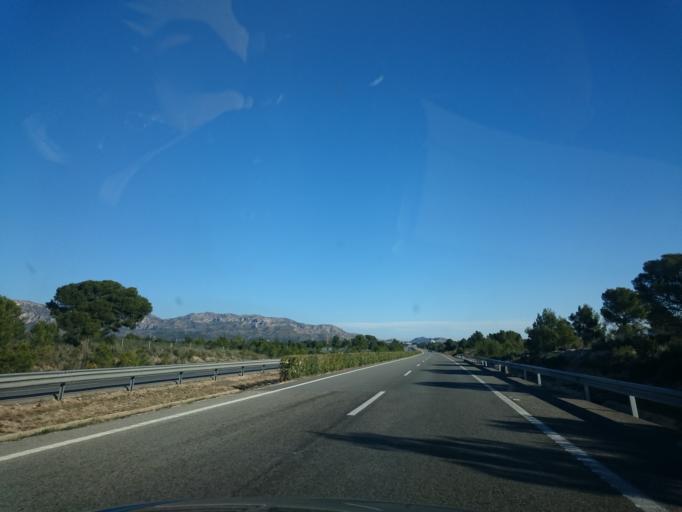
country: ES
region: Catalonia
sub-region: Provincia de Tarragona
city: l'Ametlla de Mar
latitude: 40.9096
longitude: 0.8220
